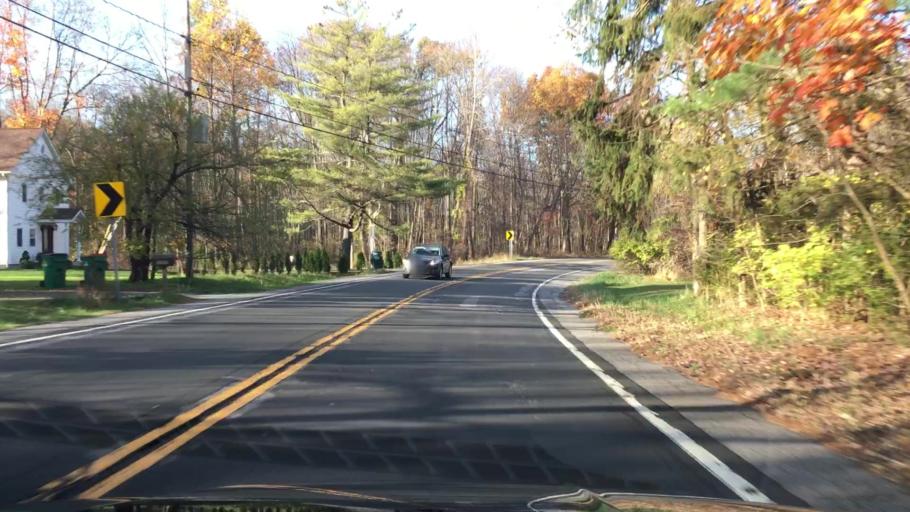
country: US
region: New York
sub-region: Dutchess County
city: Myers Corner
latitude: 41.6158
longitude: -73.8500
